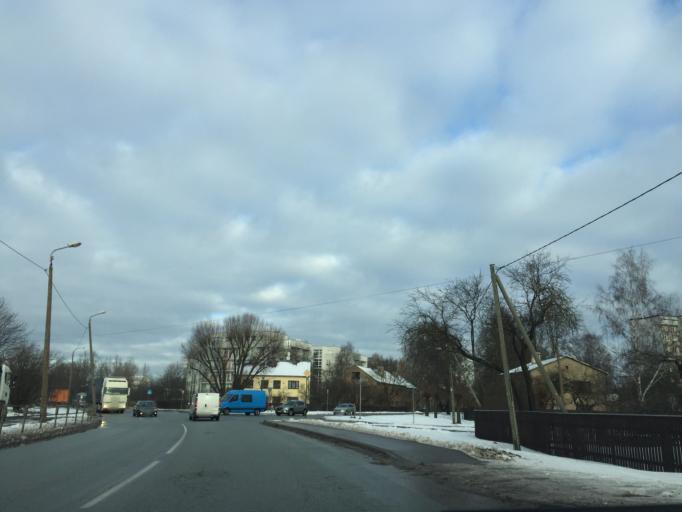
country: LV
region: Riga
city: Riga
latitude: 56.9556
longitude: 24.1653
